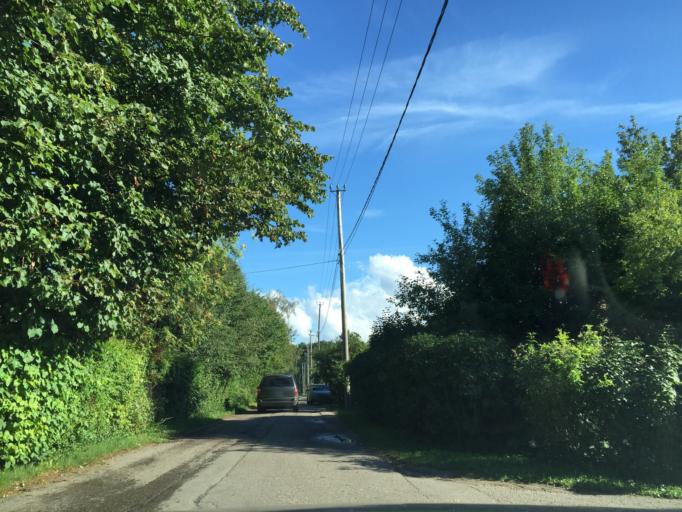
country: LV
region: Riga
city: Jaunciems
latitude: 57.0792
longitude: 24.1453
